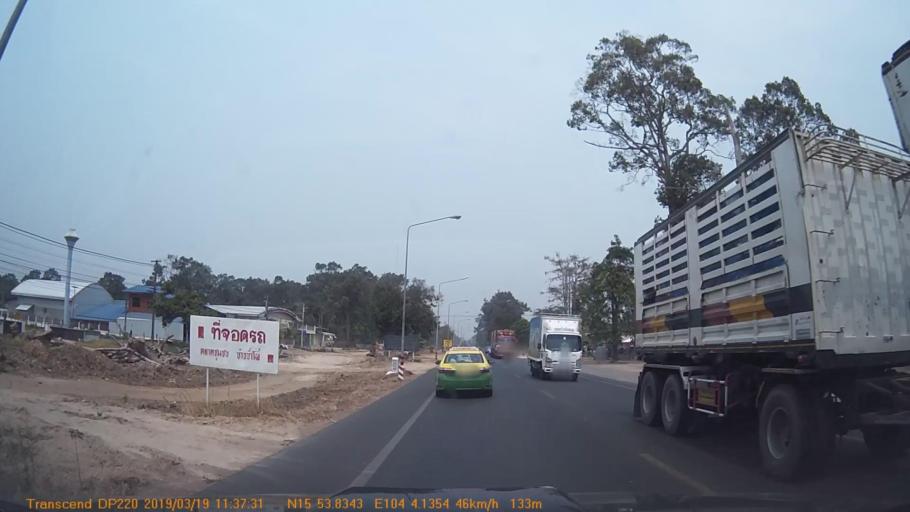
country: TH
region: Yasothon
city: Yasothon
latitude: 15.8974
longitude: 104.0688
